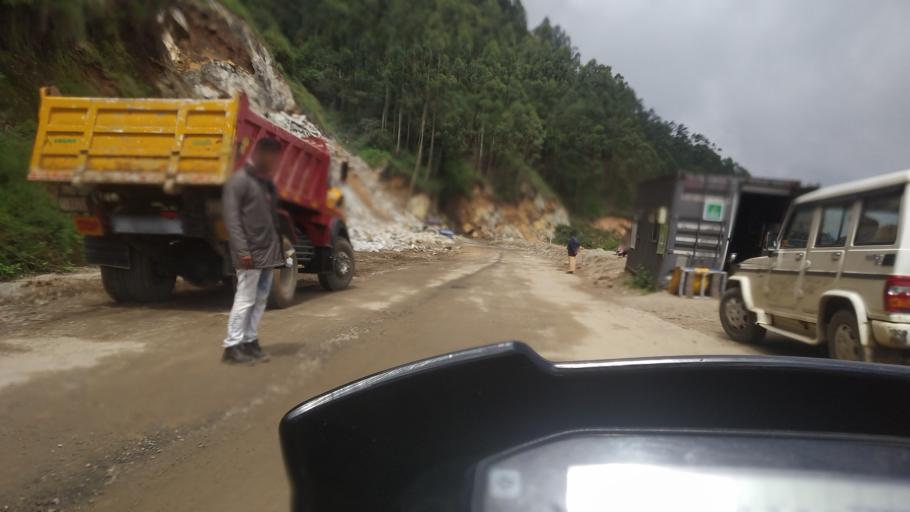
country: IN
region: Kerala
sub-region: Idukki
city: Munnar
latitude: 10.0368
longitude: 77.1318
